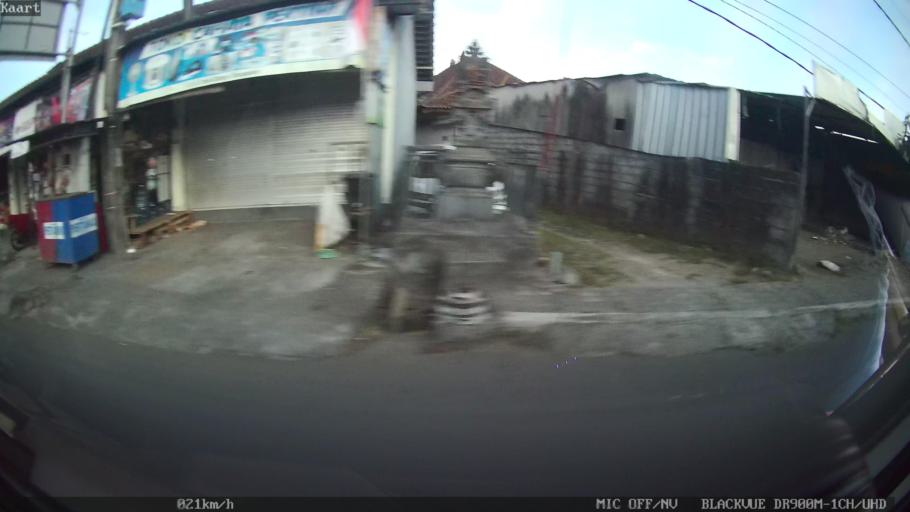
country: ID
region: Bali
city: Banjar Kertasari
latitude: -8.6199
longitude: 115.2106
